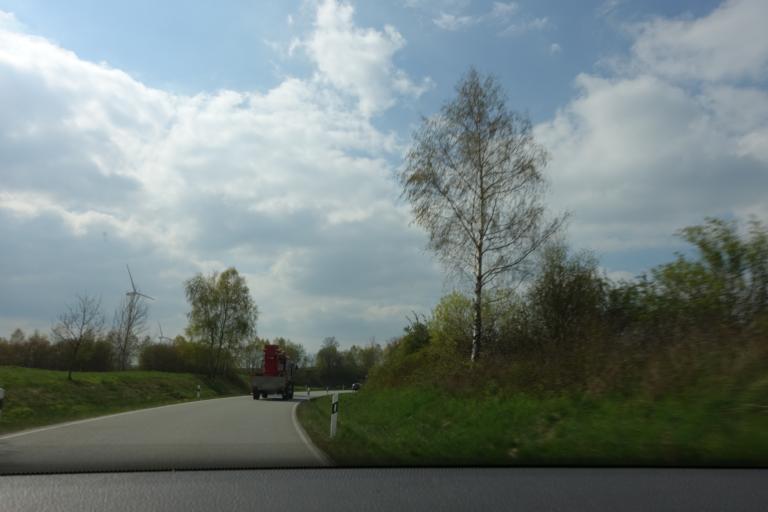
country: DE
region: Saxony
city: Gornau
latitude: 50.7515
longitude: 13.0396
